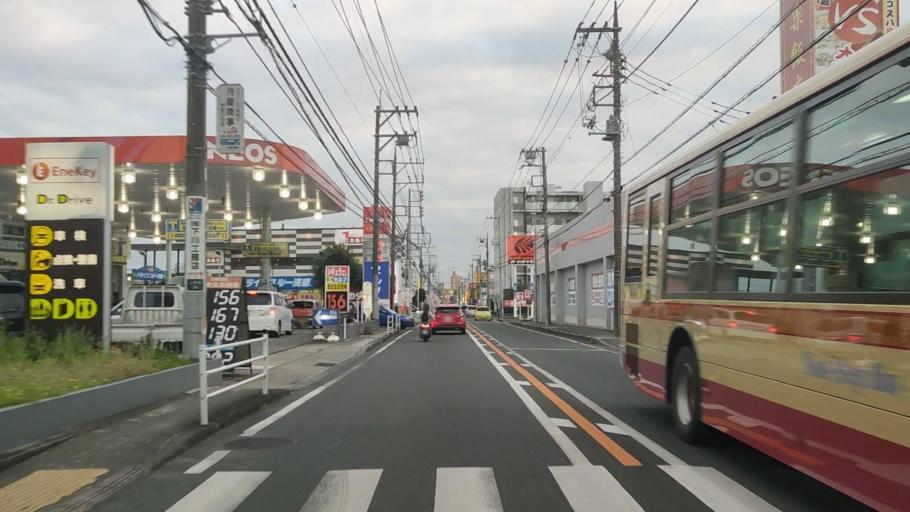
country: JP
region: Kanagawa
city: Minami-rinkan
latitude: 35.4590
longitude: 139.4673
